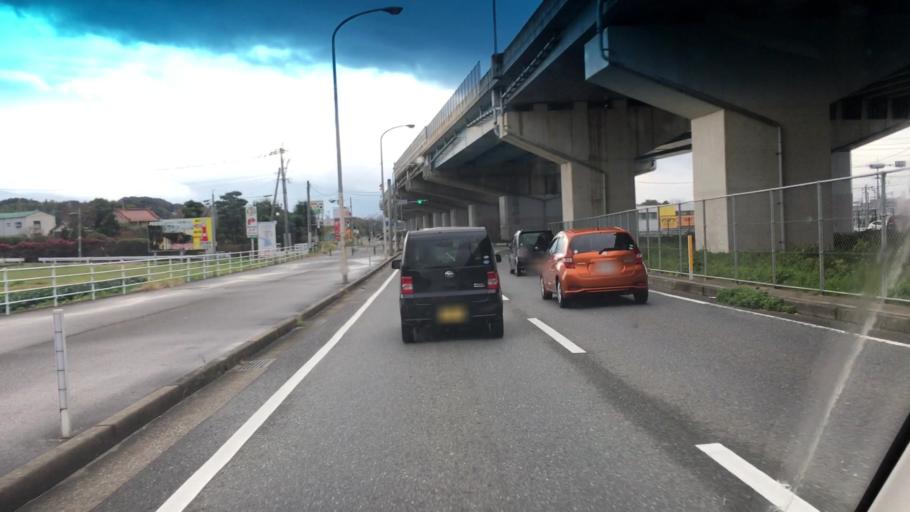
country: JP
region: Fukuoka
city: Maebaru-chuo
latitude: 33.5703
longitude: 130.2500
